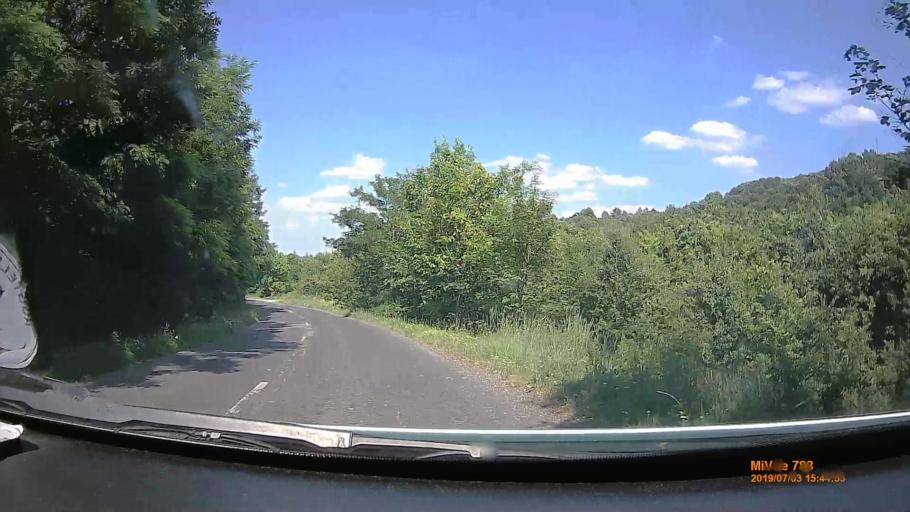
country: HU
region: Heves
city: Szilvasvarad
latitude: 48.1746
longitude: 20.4509
